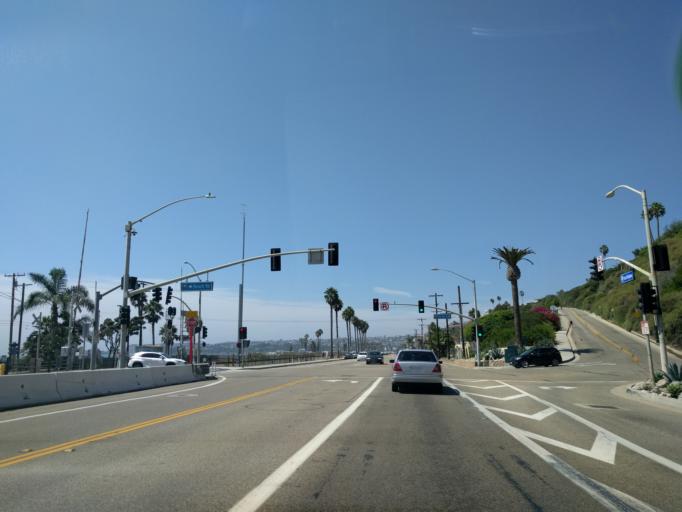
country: US
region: California
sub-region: Orange County
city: Dana Point
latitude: 33.4554
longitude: -117.6675
